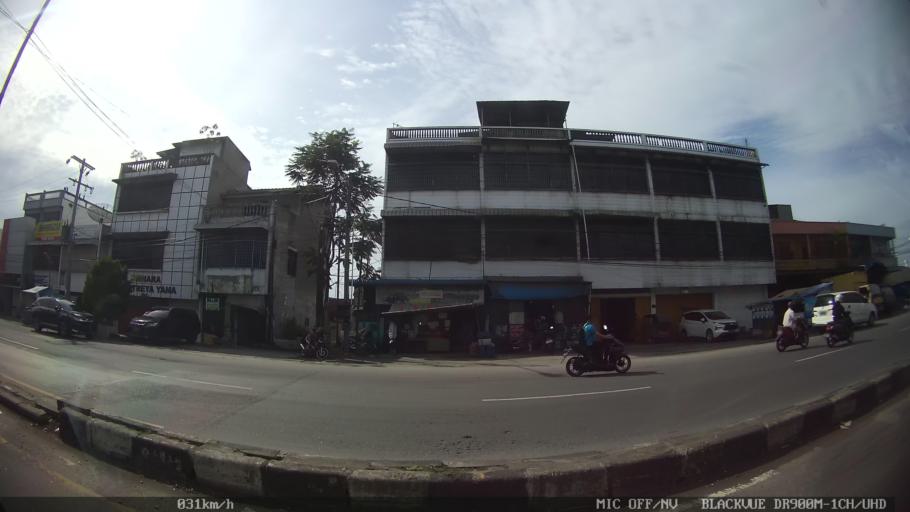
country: ID
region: North Sumatra
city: Medan
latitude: 3.6270
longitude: 98.6668
